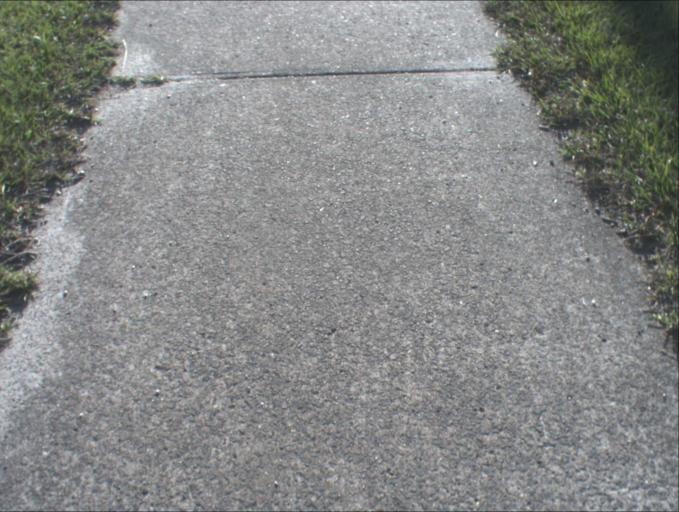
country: AU
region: Queensland
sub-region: Logan
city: Chambers Flat
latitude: -27.7665
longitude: 153.1138
